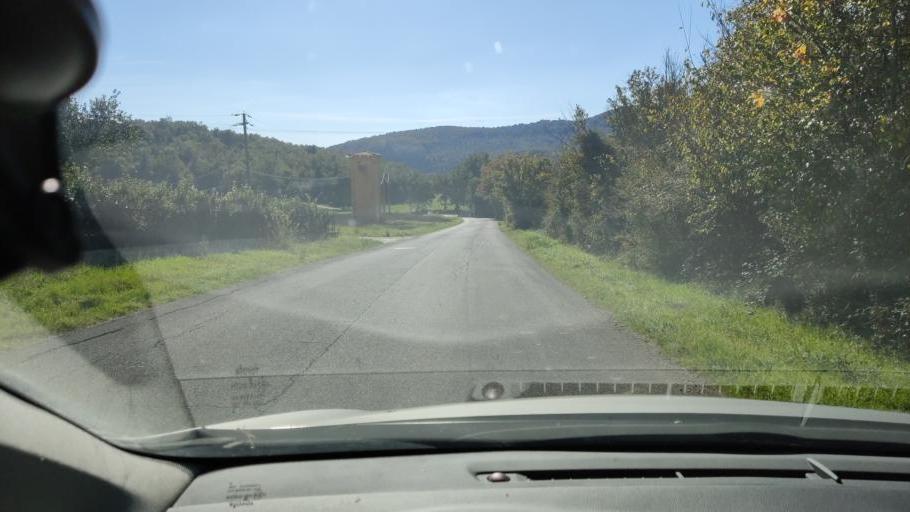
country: IT
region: Umbria
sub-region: Provincia di Terni
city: Amelia
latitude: 42.5964
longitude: 12.4370
